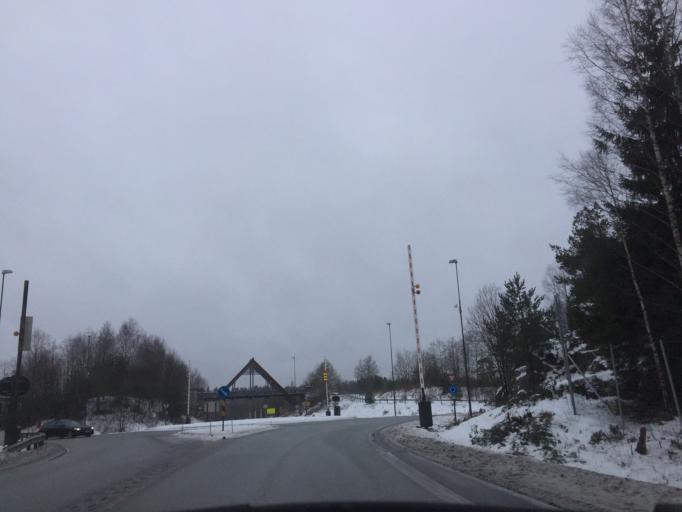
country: NO
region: Akershus
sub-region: Frogn
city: Drobak
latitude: 59.6952
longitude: 10.6611
